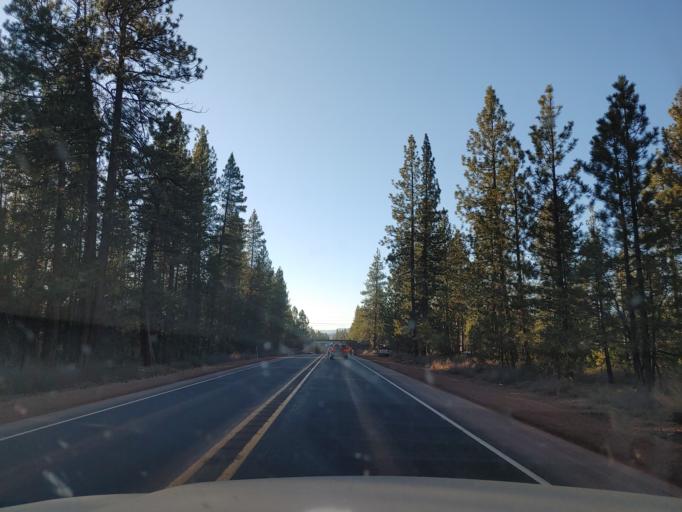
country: US
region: Oregon
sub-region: Deschutes County
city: La Pine
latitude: 43.3755
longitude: -121.7963
